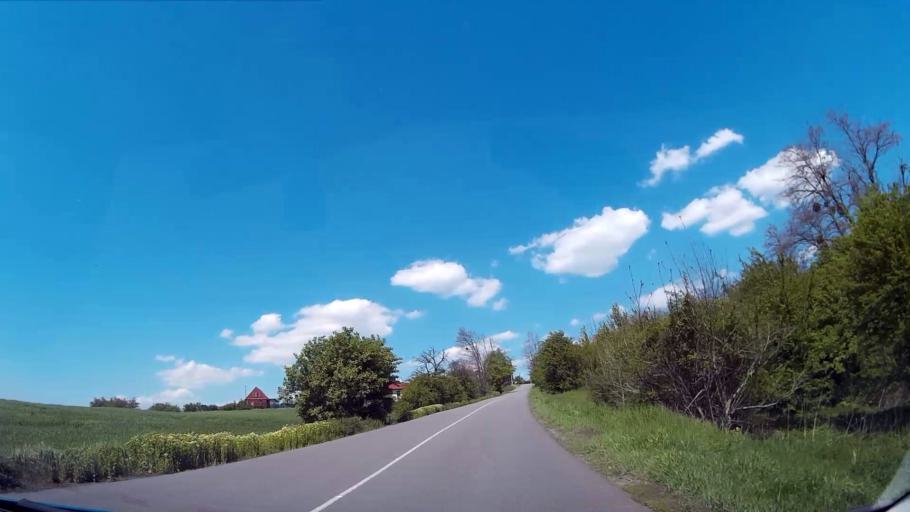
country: CZ
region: South Moravian
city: Zbysov
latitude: 49.1521
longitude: 16.3799
